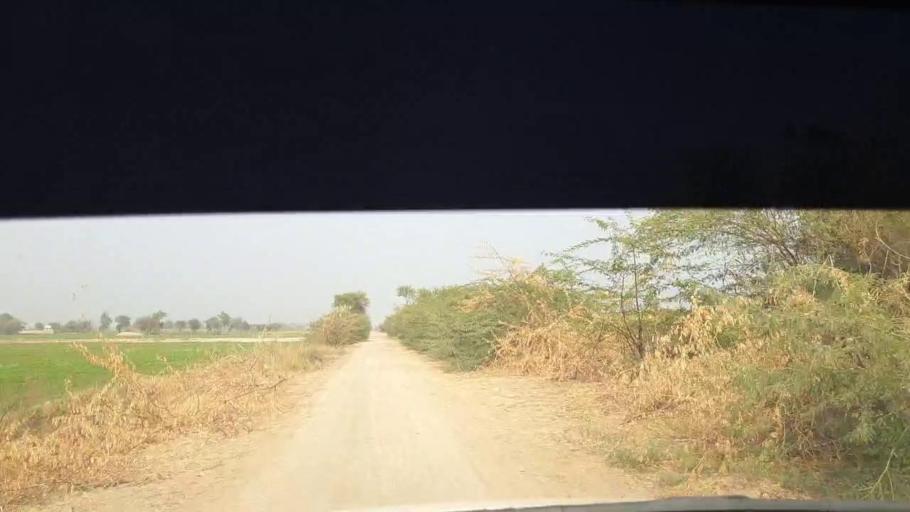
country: PK
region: Sindh
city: Berani
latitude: 25.8290
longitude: 68.8352
